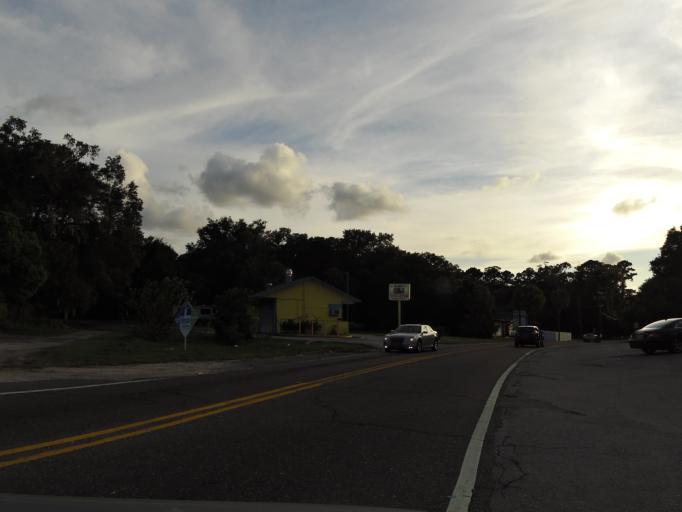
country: US
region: Florida
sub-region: Duval County
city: Jacksonville
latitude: 30.4153
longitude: -81.6958
